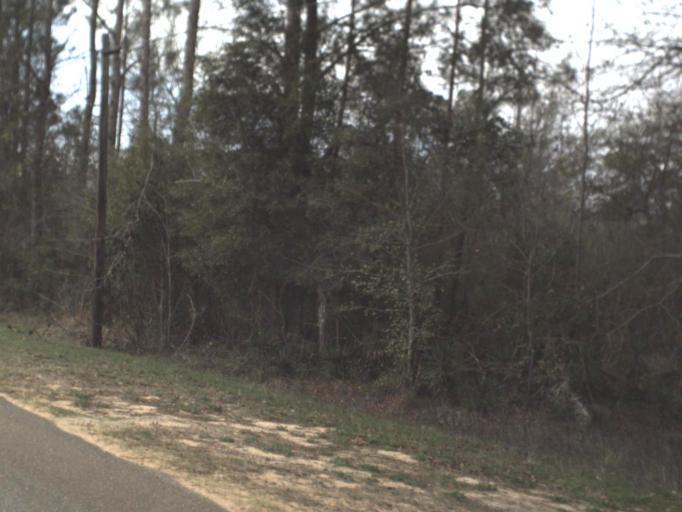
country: US
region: Florida
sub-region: Liberty County
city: Bristol
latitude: 30.4511
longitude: -84.9687
